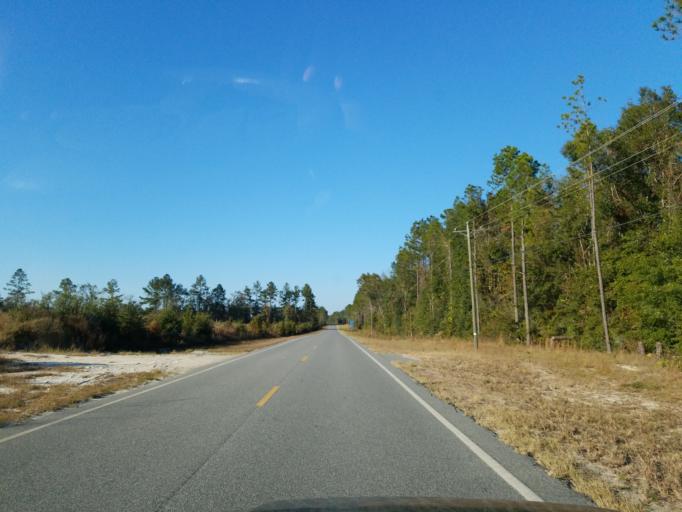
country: US
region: Georgia
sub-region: Echols County
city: Statenville
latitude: 30.6810
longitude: -83.0604
